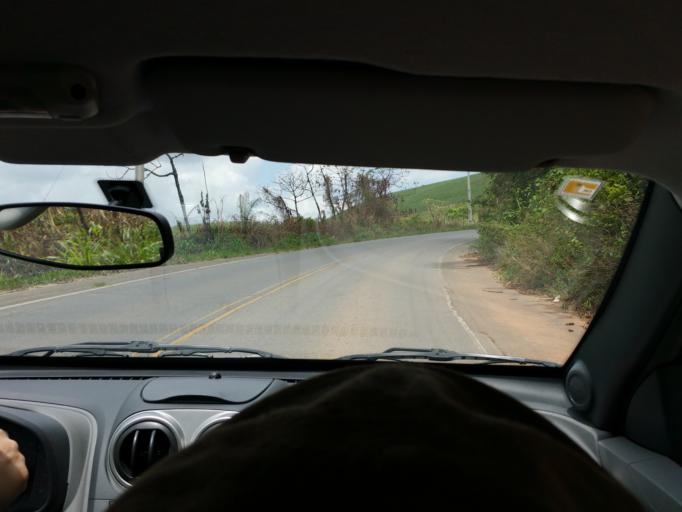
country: BR
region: Pernambuco
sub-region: Sirinhaem
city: Sirinhaem
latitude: -8.6223
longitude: -35.1263
